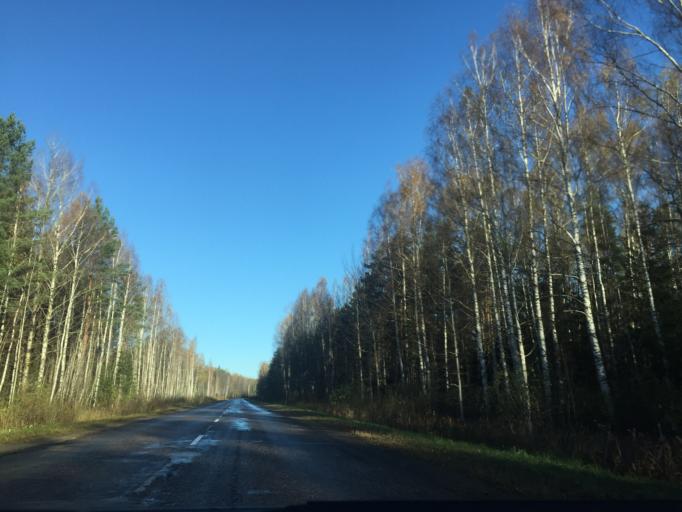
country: LV
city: Tireli
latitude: 56.9130
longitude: 23.5261
